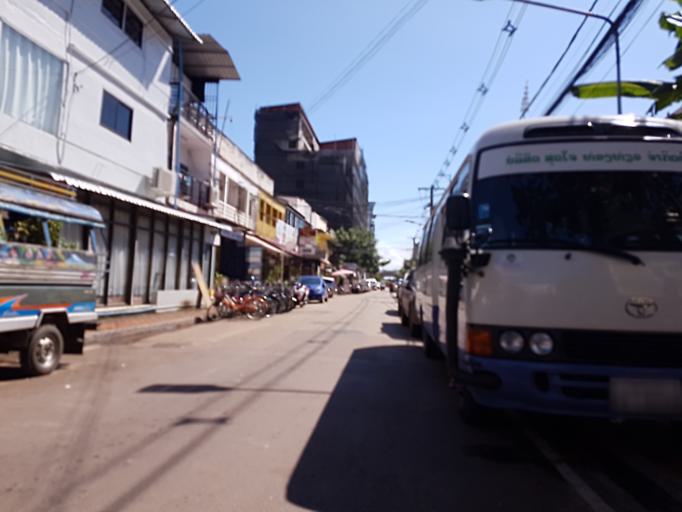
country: LA
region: Vientiane
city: Vientiane
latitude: 17.9652
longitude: 102.6057
